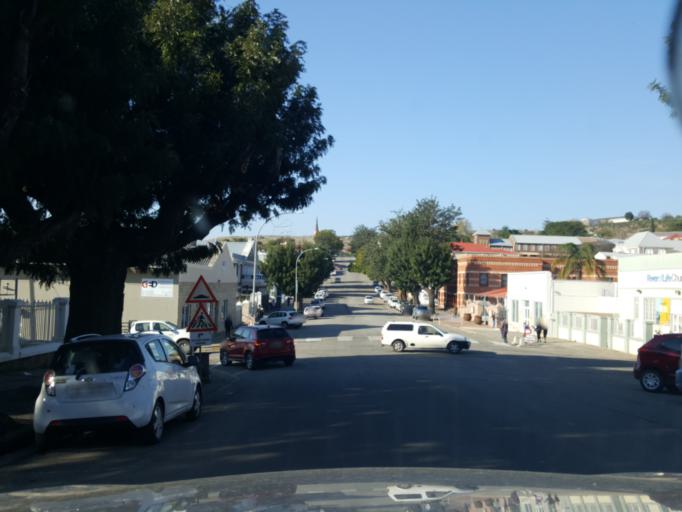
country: ZA
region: Eastern Cape
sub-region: Cacadu District Municipality
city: Grahamstown
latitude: -33.3113
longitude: 26.5274
